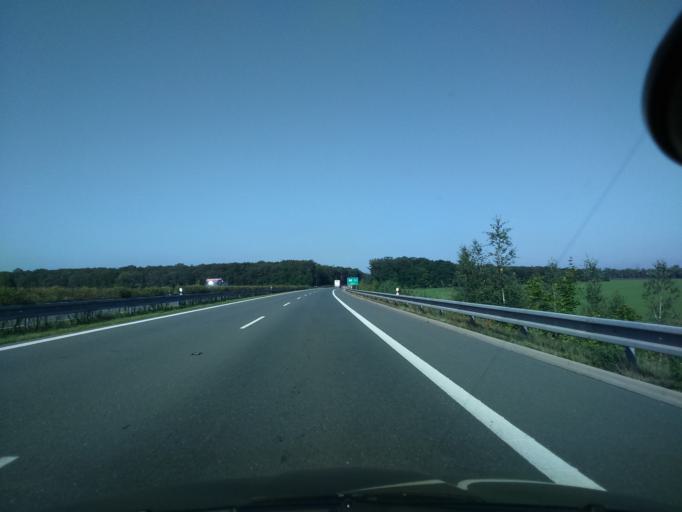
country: CZ
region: Pardubicky
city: Opatovice nad Labem
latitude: 50.1408
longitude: 15.7734
